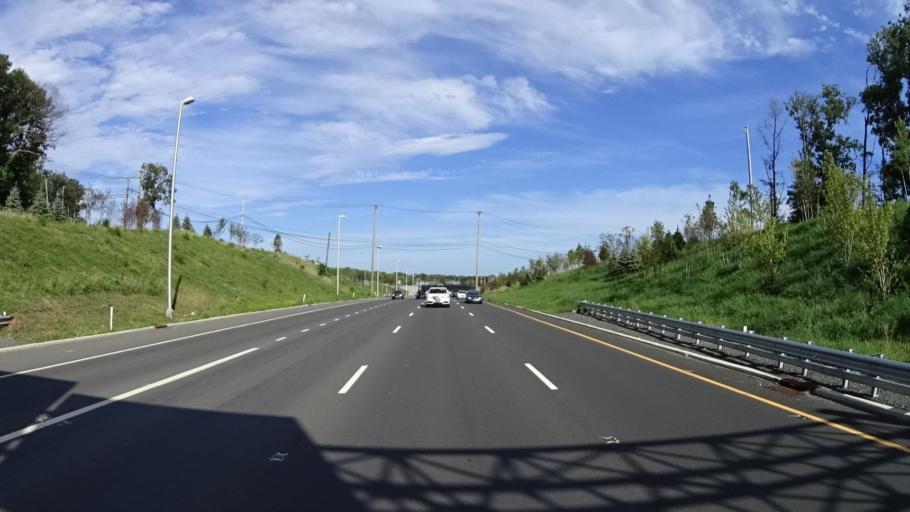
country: US
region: New Jersey
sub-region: Somerset County
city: Finderne
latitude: 40.5759
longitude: -74.5654
